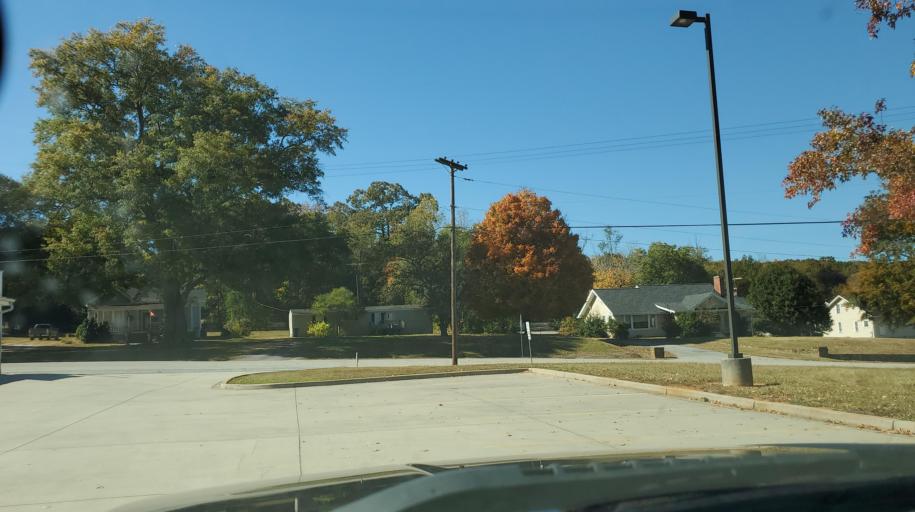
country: US
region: South Carolina
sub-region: Greenville County
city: Tigerville
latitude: 35.0725
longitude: -82.3686
